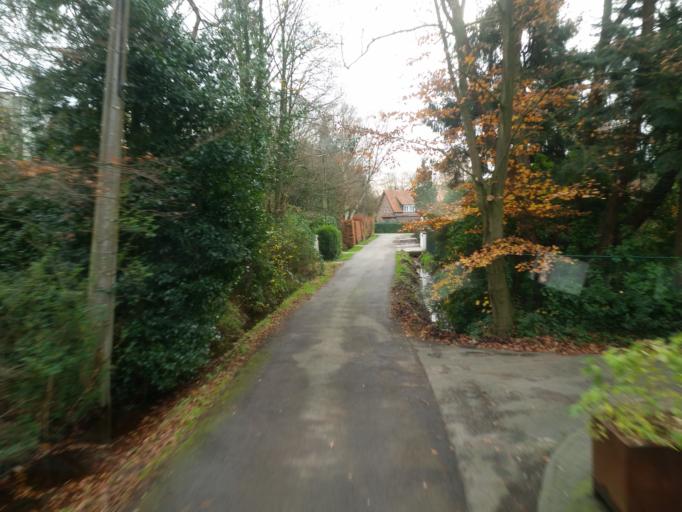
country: BE
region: Flanders
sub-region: Provincie Antwerpen
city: Kalmthout
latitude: 51.3893
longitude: 4.4545
